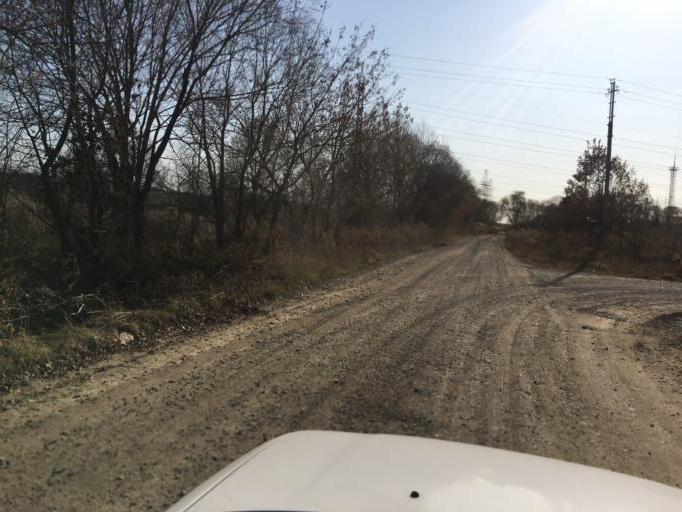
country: RU
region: Primorskiy
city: Dal'nerechensk
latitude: 45.9155
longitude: 133.7148
